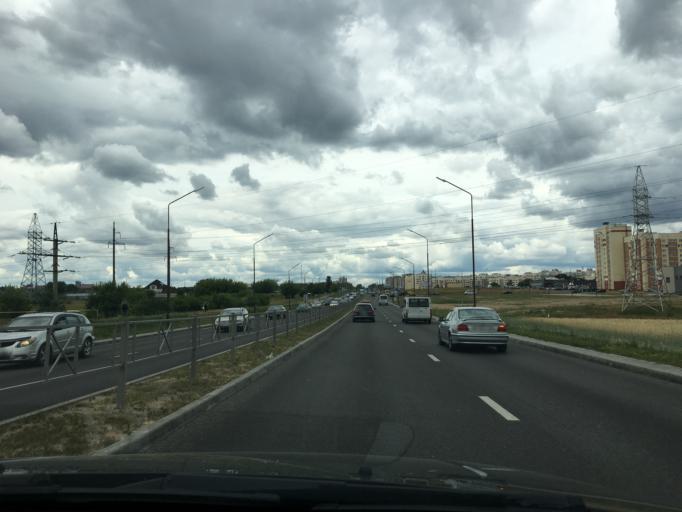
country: BY
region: Grodnenskaya
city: Hrodna
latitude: 53.6324
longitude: 23.8536
